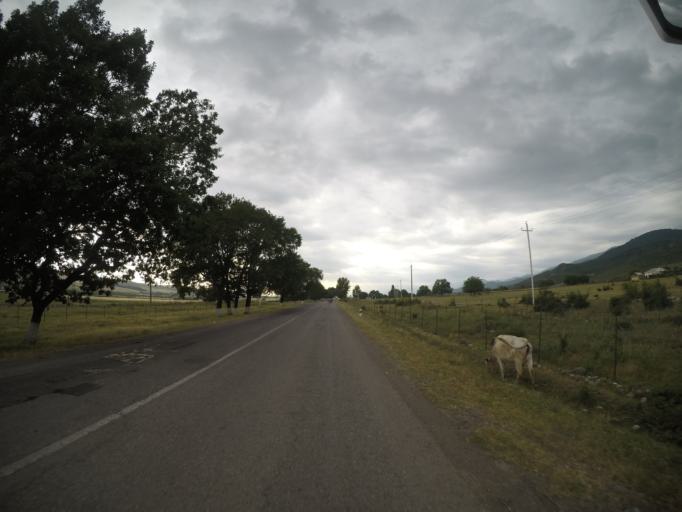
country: AZ
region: Ismayilli
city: Ismayilli
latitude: 40.7589
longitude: 48.2169
